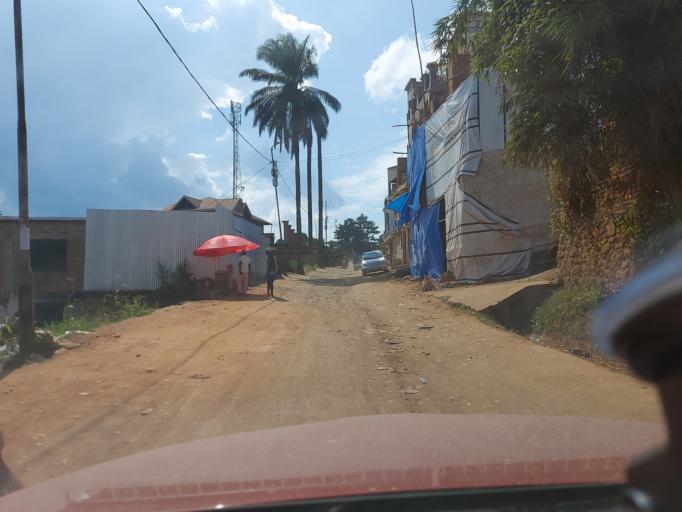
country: CD
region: South Kivu
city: Bukavu
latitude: -2.4985
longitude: 28.8670
